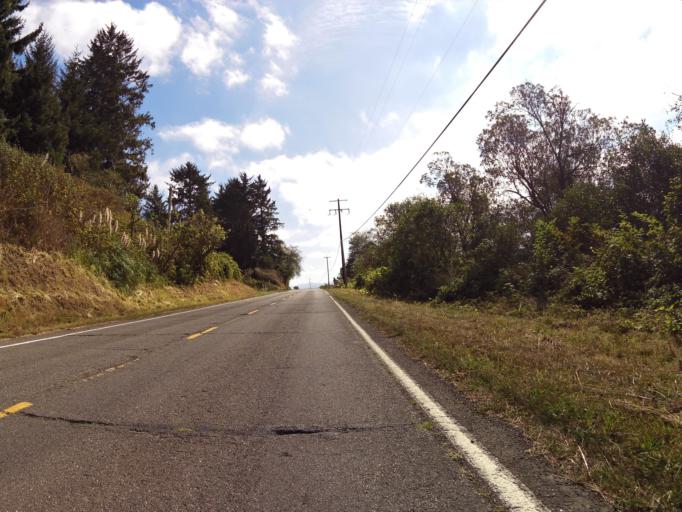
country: US
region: California
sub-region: Humboldt County
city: Ferndale
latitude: 40.6315
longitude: -124.2220
